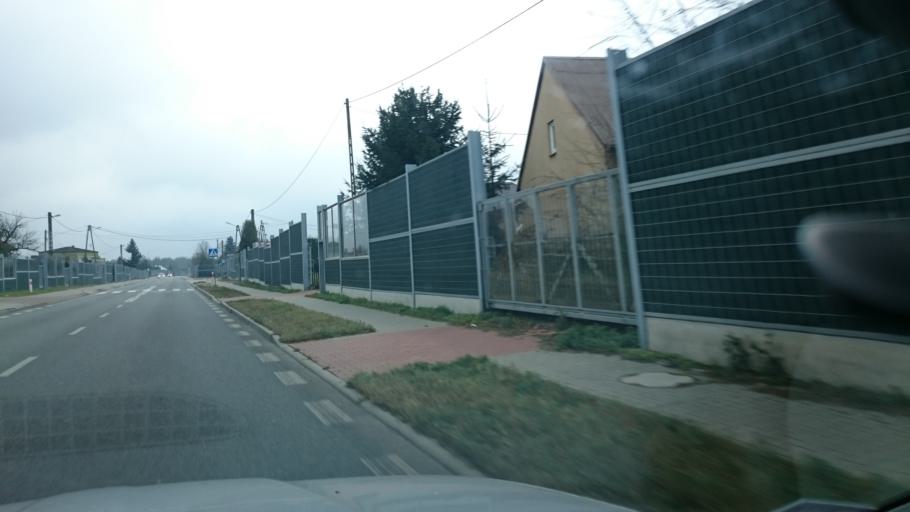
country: PL
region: Swietokrzyskie
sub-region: Powiat konecki
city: Konskie
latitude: 51.1449
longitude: 20.3632
